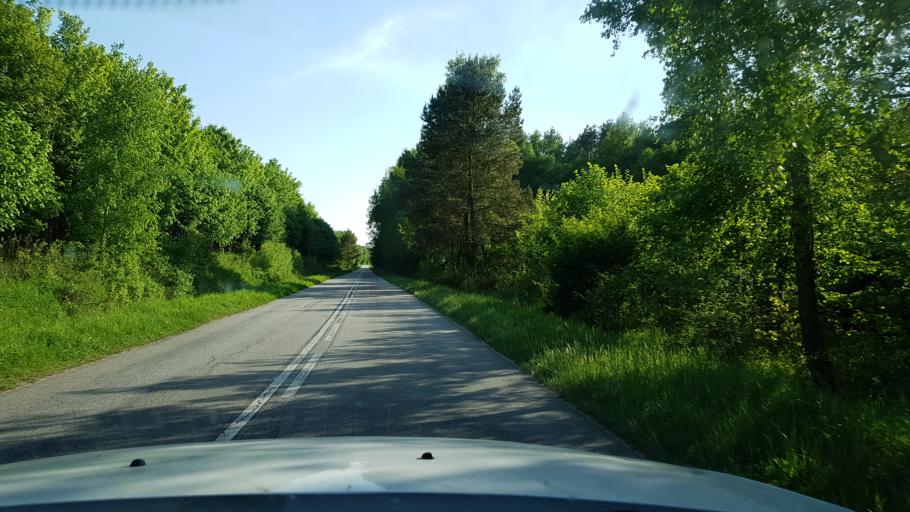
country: PL
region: West Pomeranian Voivodeship
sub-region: Powiat lobeski
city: Resko
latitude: 53.7561
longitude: 15.3775
